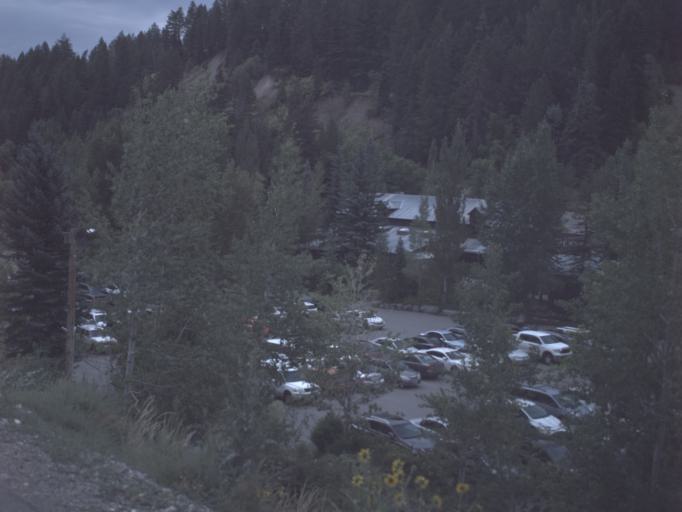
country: US
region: Utah
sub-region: Utah County
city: Orem
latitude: 40.3924
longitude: -111.5781
